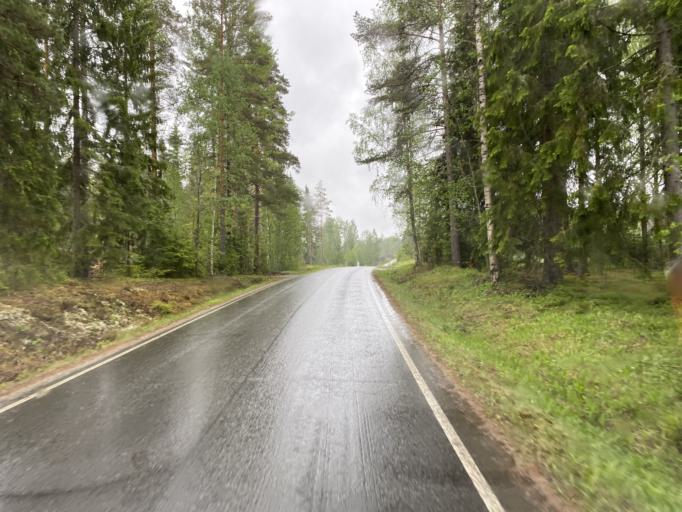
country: FI
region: Haeme
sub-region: Forssa
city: Humppila
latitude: 61.0838
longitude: 23.3108
